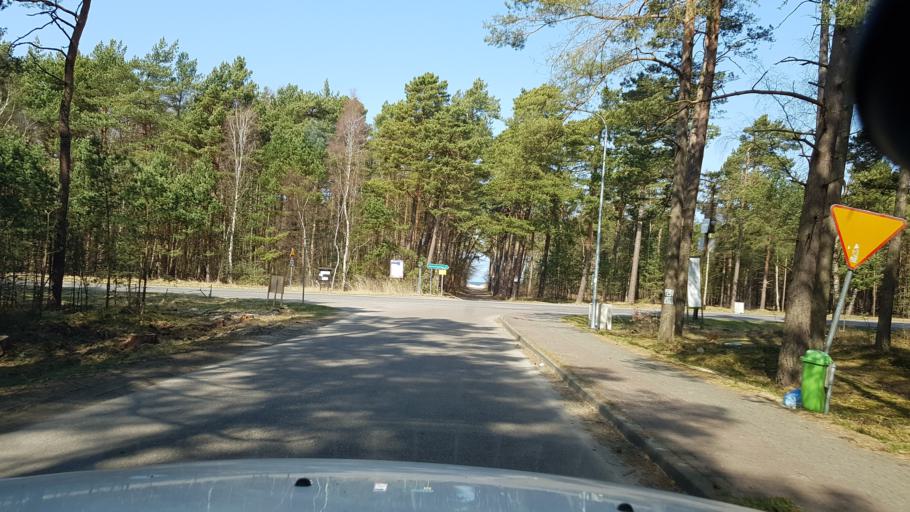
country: PL
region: West Pomeranian Voivodeship
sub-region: Powiat slawienski
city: Darlowo
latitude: 54.5257
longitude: 16.5097
